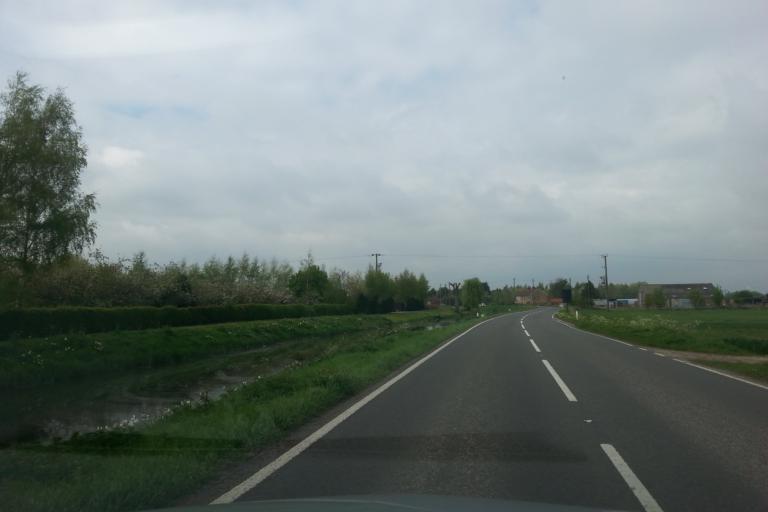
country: GB
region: England
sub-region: Norfolk
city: Outwell
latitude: 52.6061
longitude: 0.2493
